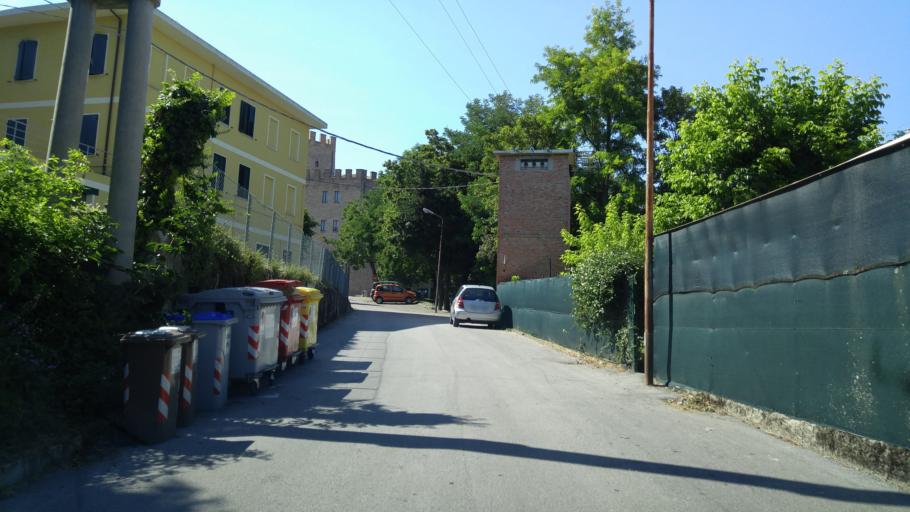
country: IT
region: The Marches
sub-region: Provincia di Pesaro e Urbino
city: Monteciccardo
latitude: 43.8263
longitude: 12.8036
